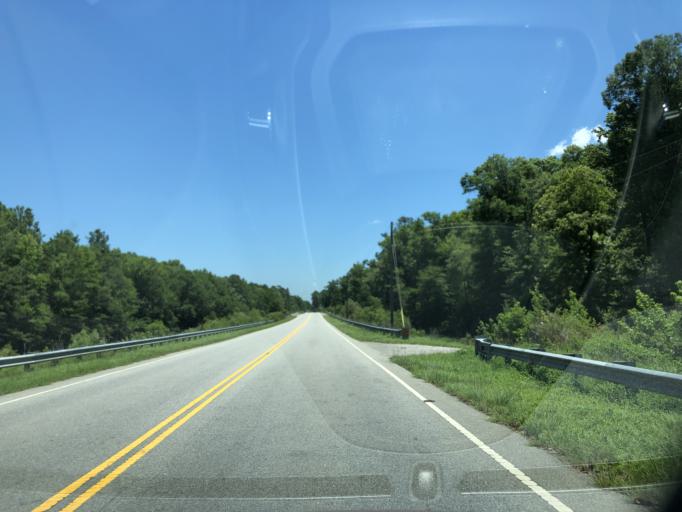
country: US
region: South Carolina
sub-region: Orangeburg County
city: Branchville
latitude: 33.2422
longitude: -80.8530
